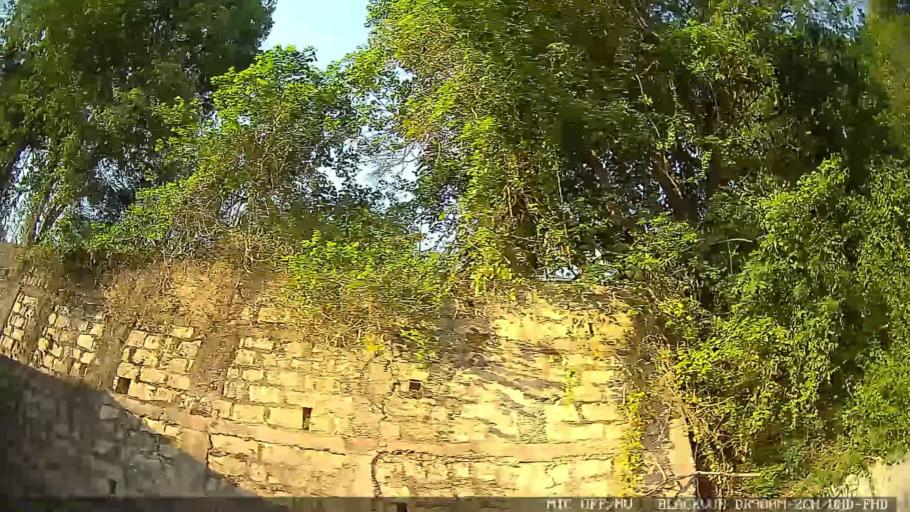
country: BR
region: Sao Paulo
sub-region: Itatiba
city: Itatiba
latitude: -23.0071
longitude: -46.8406
